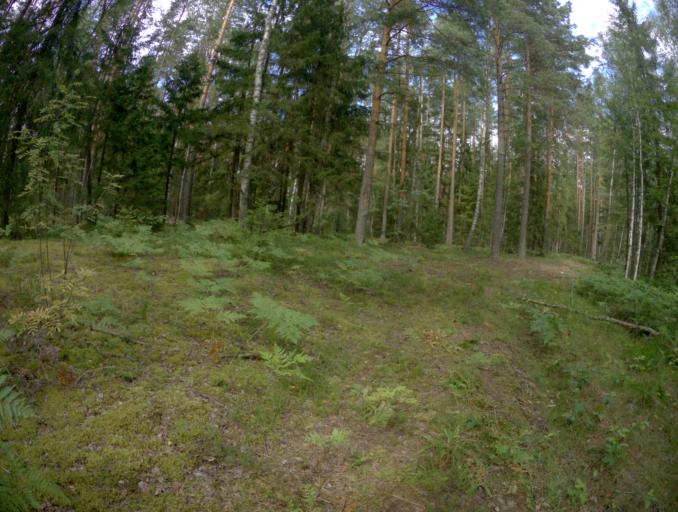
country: RU
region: Vladimir
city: Orgtrud
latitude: 56.0763
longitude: 40.6058
